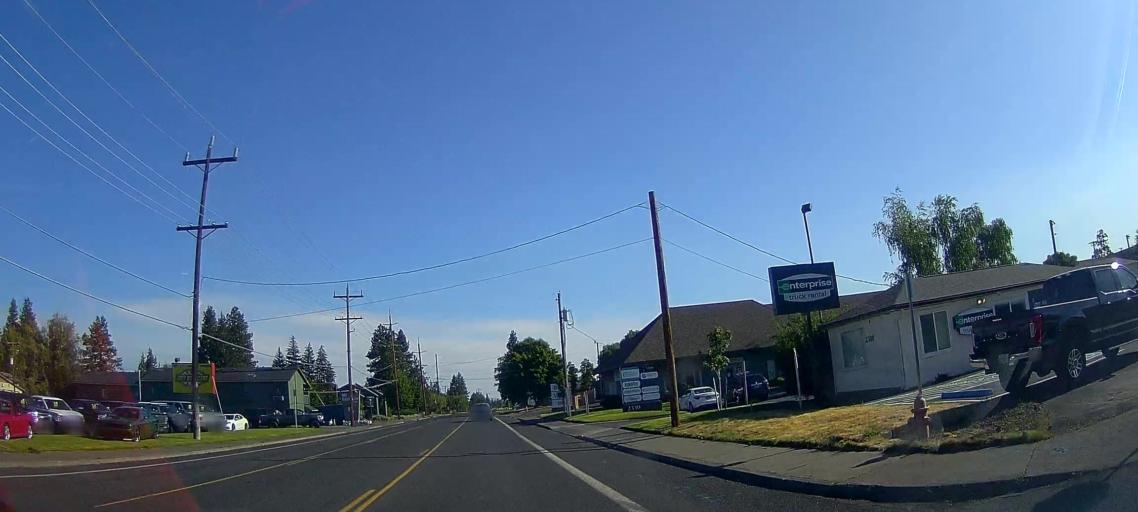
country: US
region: Oregon
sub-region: Deschutes County
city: Bend
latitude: 44.0727
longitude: -121.3060
